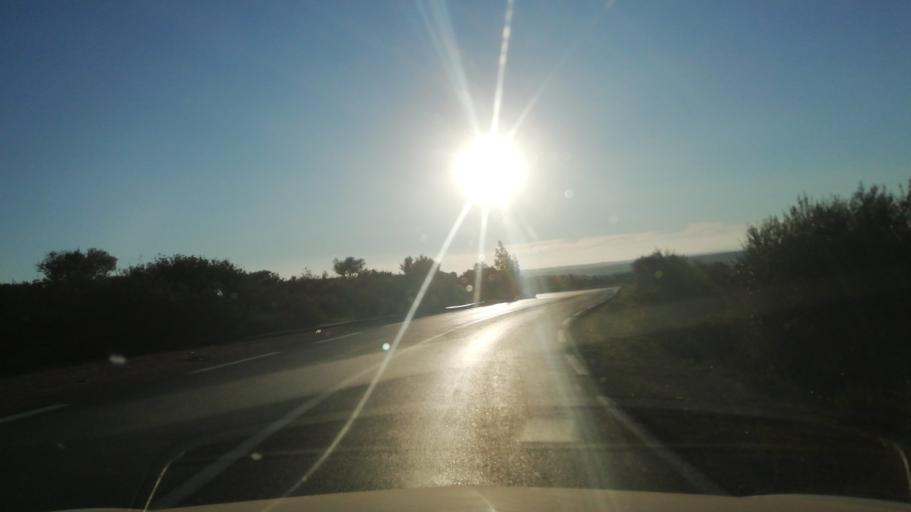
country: DZ
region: Tlemcen
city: Beni Mester
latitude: 34.8146
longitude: -1.6198
